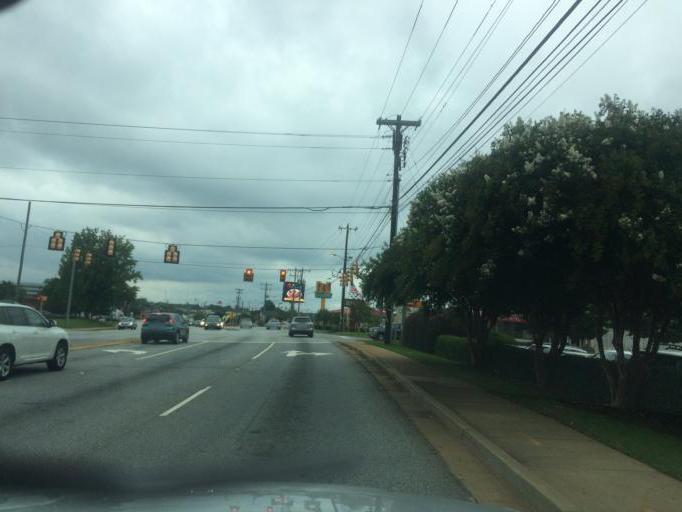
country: US
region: South Carolina
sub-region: Greenville County
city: Five Forks
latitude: 34.8596
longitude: -82.2664
